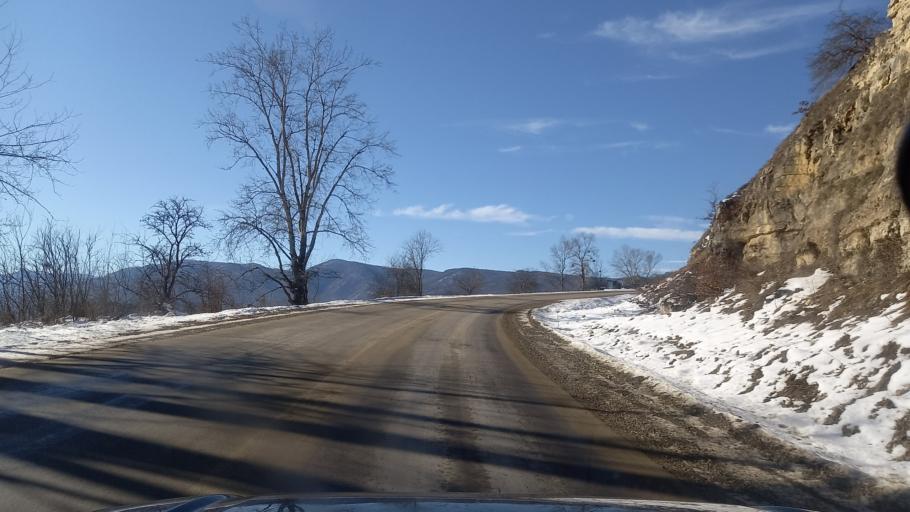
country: RU
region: Adygeya
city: Kamennomostskiy
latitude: 44.2377
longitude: 40.1594
